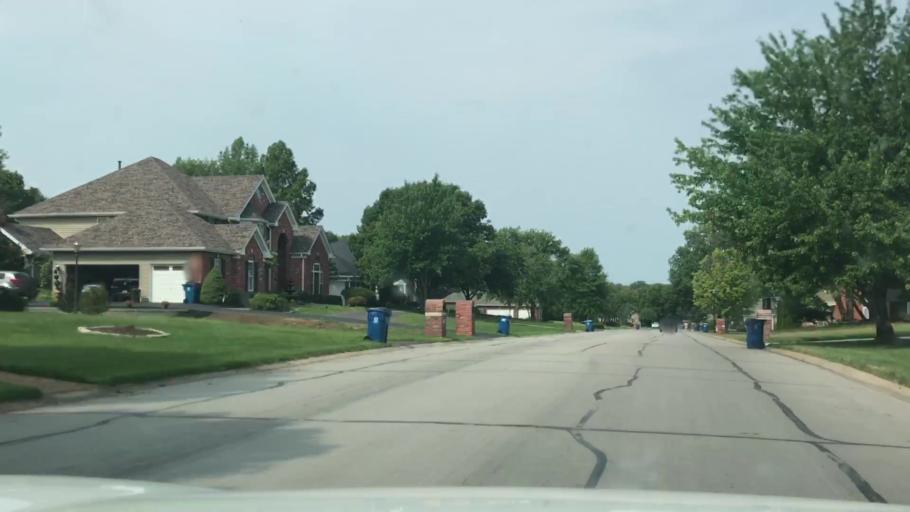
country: US
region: Missouri
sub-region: Saint Charles County
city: Cottleville
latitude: 38.7125
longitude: -90.6352
